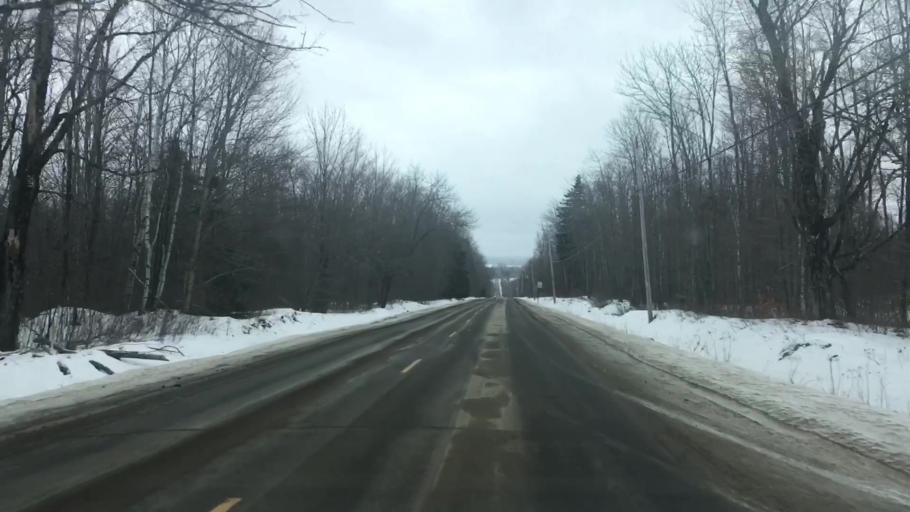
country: US
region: Maine
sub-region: Washington County
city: East Machias
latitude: 44.9765
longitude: -67.4513
